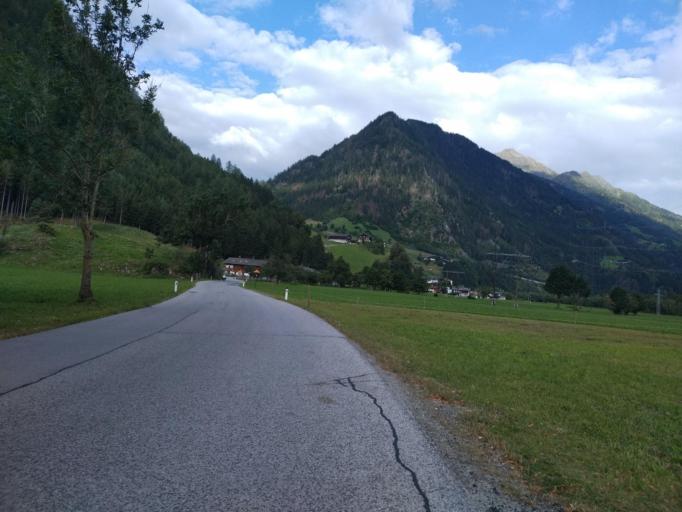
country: AT
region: Tyrol
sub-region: Politischer Bezirk Lienz
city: Hopfgarten in Defereggen
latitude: 46.9251
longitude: 12.5888
